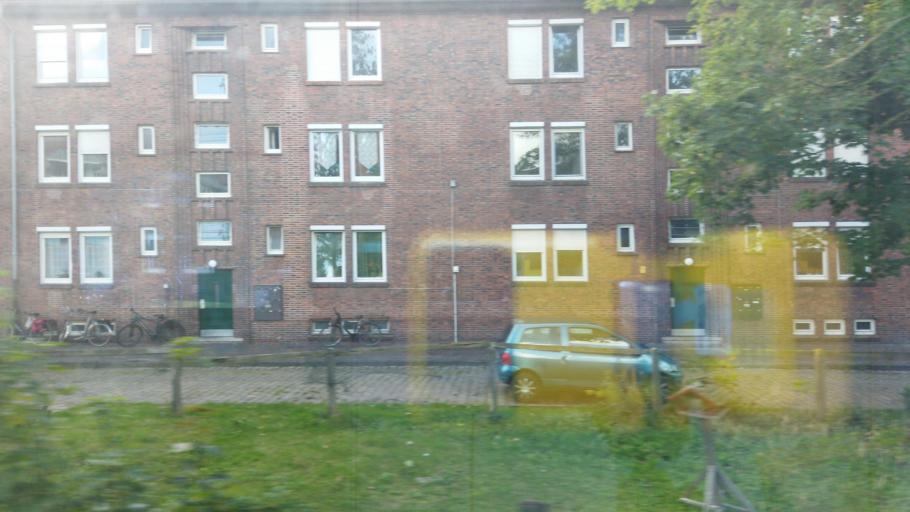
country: DE
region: Lower Saxony
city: Emden
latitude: 53.3621
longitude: 7.2013
